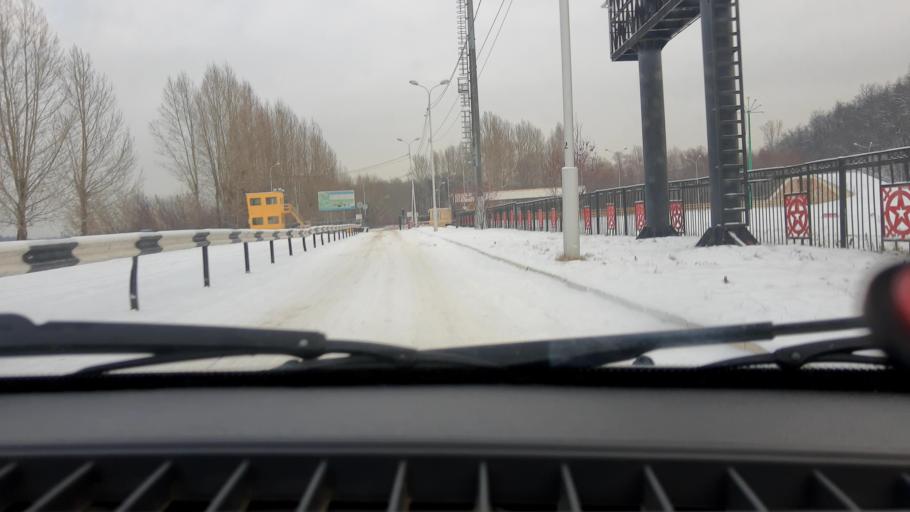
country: RU
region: Bashkortostan
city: Ufa
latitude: 54.8068
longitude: 56.0358
